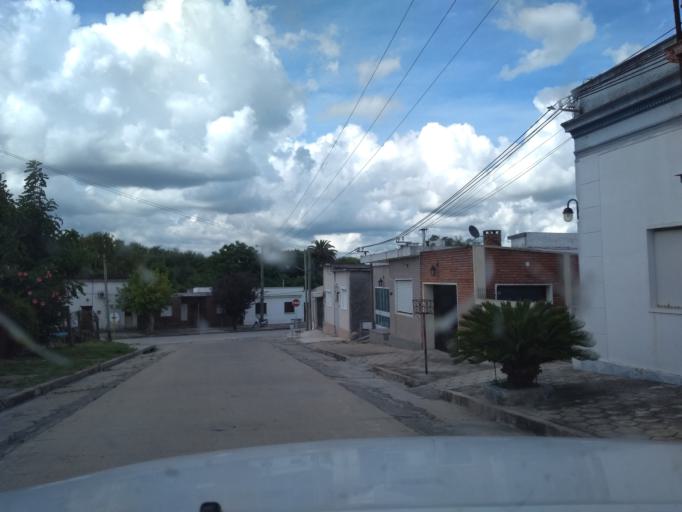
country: UY
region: Florida
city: Florida
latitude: -34.0920
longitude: -56.2141
